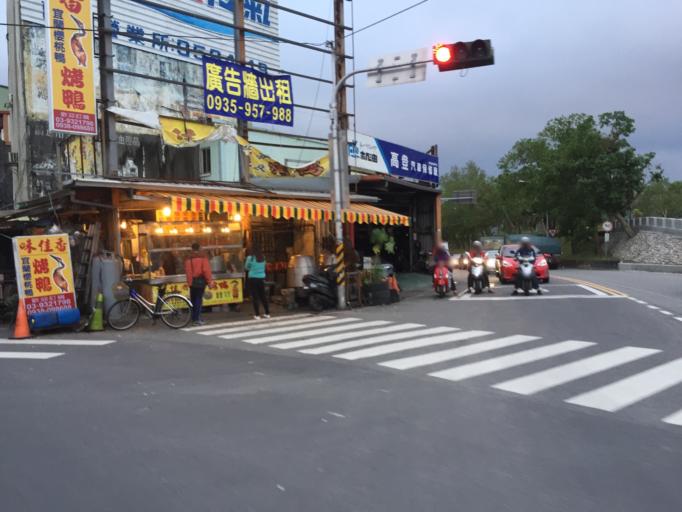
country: TW
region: Taiwan
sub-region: Yilan
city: Yilan
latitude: 24.7646
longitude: 121.7548
